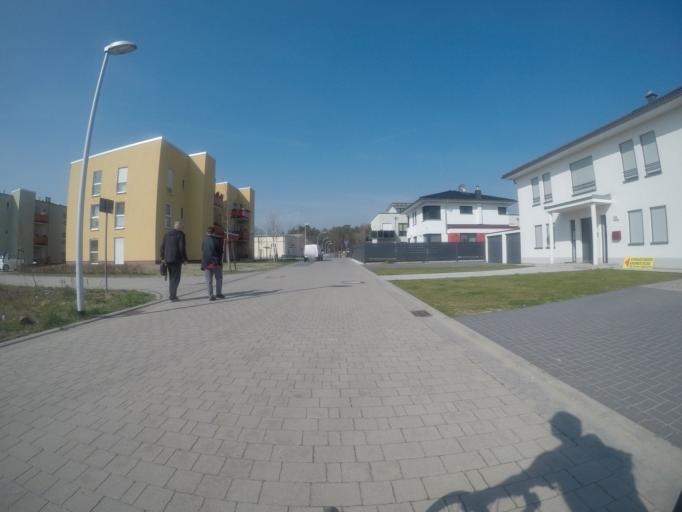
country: DE
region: Brandenburg
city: Konigs Wusterhausen
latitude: 52.2956
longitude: 13.6841
